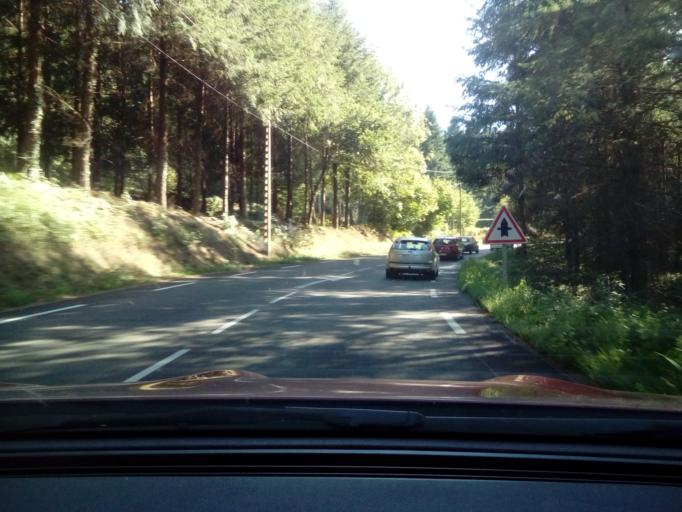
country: FR
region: Rhone-Alpes
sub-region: Departement du Rhone
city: Cublize
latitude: 45.9719
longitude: 4.3928
